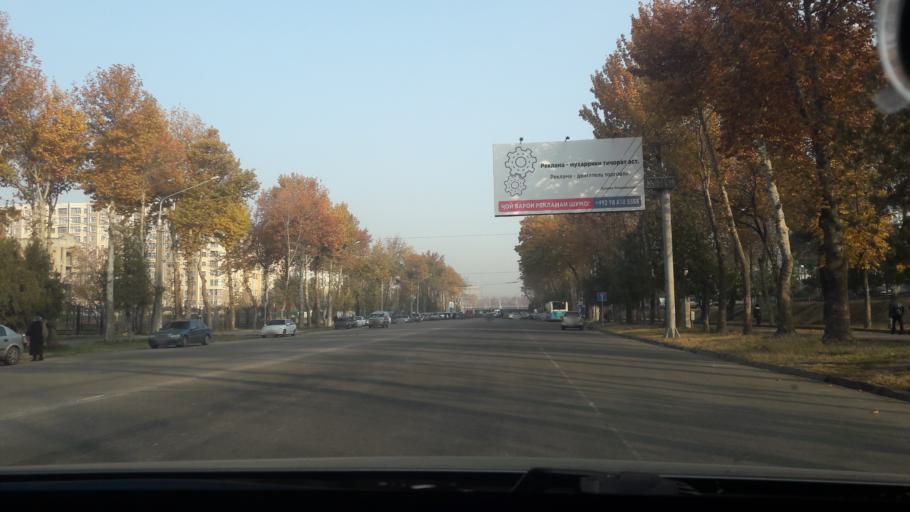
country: TJ
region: Dushanbe
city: Dushanbe
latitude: 38.5786
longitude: 68.7550
